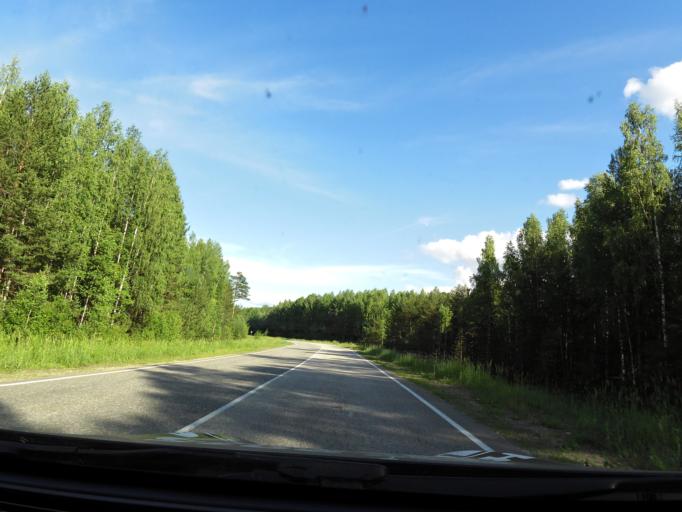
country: RU
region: Kirov
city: Chernaya Kholunitsa
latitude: 58.8310
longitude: 51.7605
